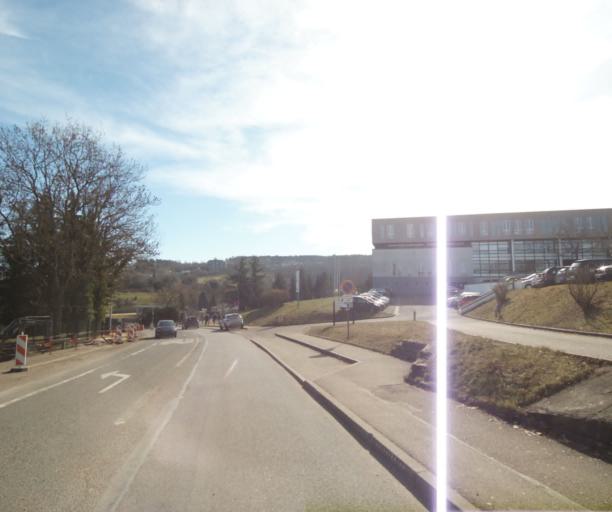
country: FR
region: Lorraine
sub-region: Departement de Meurthe-et-Moselle
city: Villers-les-Nancy
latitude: 48.6639
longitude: 6.1526
